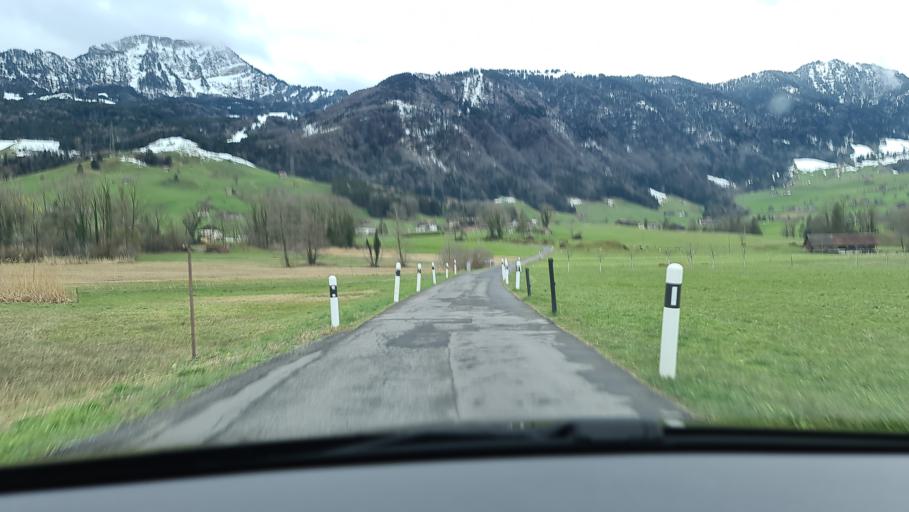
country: CH
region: Schwyz
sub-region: Bezirk Schwyz
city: Goldau
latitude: 47.0417
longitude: 8.5766
